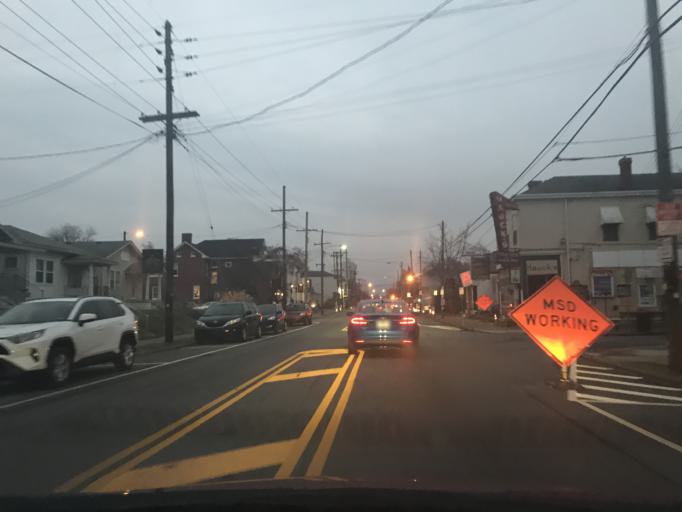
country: US
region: Kentucky
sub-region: Jefferson County
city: Audubon Park
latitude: 38.2280
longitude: -85.7366
